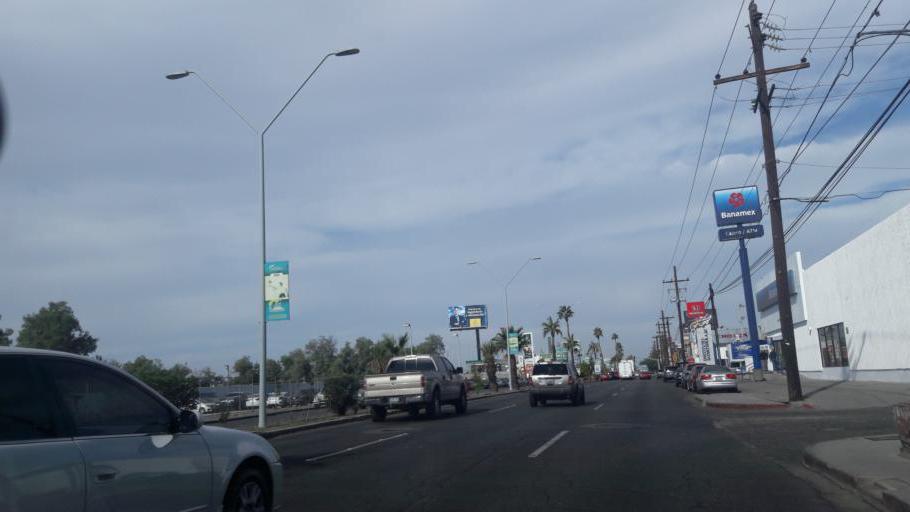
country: MX
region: Baja California
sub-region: Mexicali
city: Mexicali
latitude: 32.6513
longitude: -115.4523
